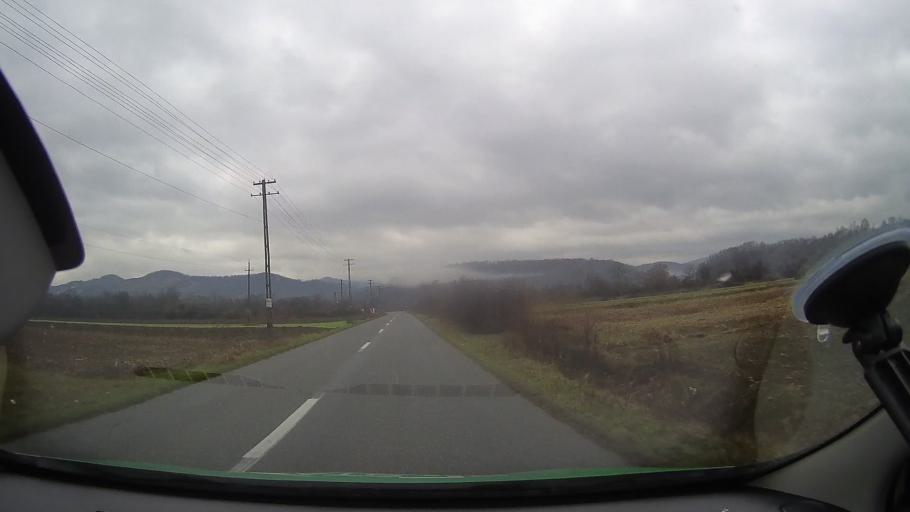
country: RO
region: Arad
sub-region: Comuna Brazii
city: Brazii
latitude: 46.2437
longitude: 22.3309
